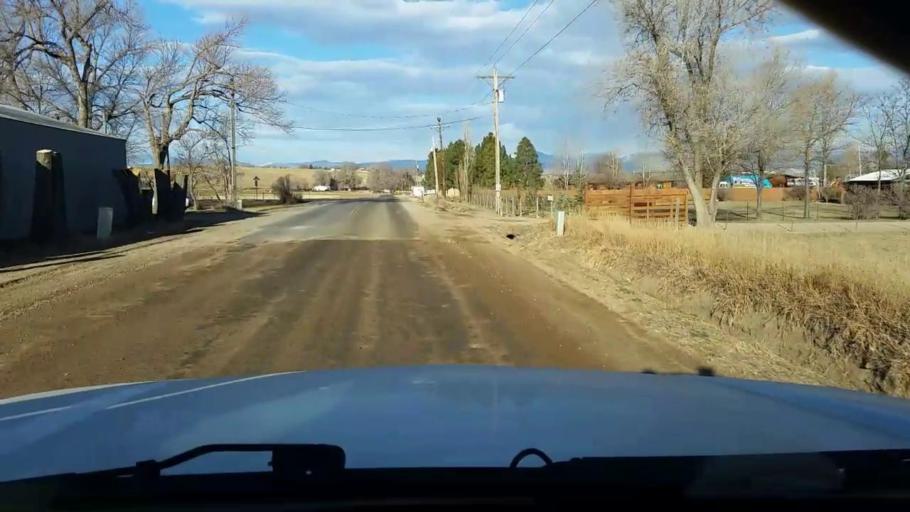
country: US
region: Colorado
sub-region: Larimer County
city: Campion
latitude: 40.3712
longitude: -105.0584
